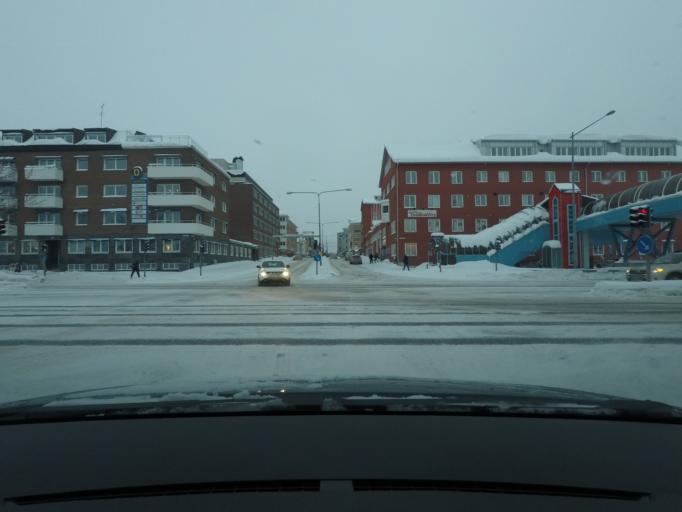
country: SE
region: Norrbotten
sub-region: Lulea Kommun
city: Lulea
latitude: 65.5811
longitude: 22.1542
